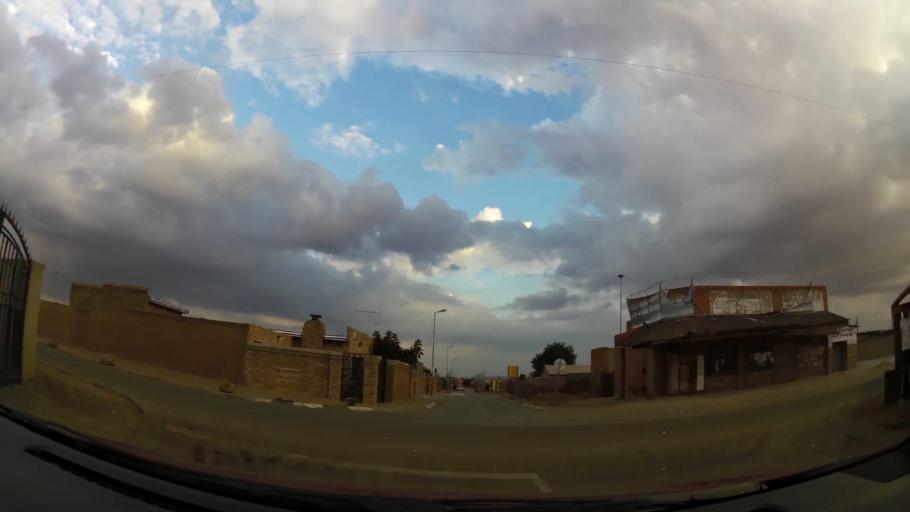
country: ZA
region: Gauteng
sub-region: City of Johannesburg Metropolitan Municipality
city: Soweto
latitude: -26.2467
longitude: 27.8305
